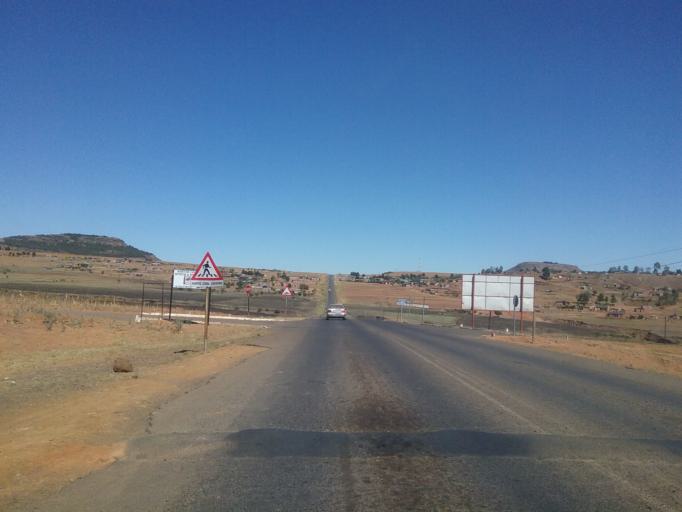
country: LS
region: Quthing
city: Quthing
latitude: -30.3968
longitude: 27.6488
